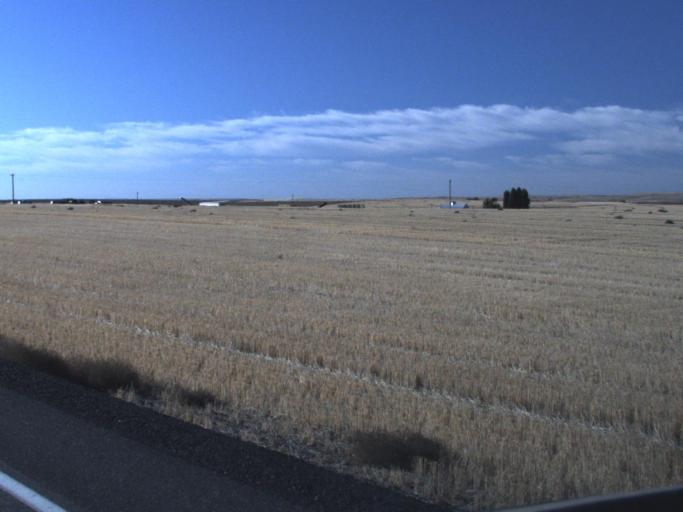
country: US
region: Washington
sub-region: Walla Walla County
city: Garrett
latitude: 46.2964
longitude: -118.6315
